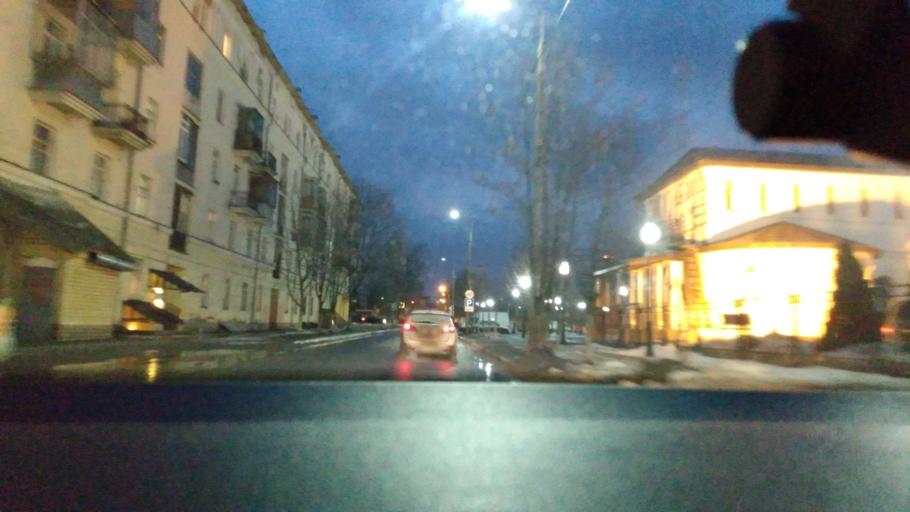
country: RU
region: Moskovskaya
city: Saltykovka
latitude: 55.7970
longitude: 37.9291
